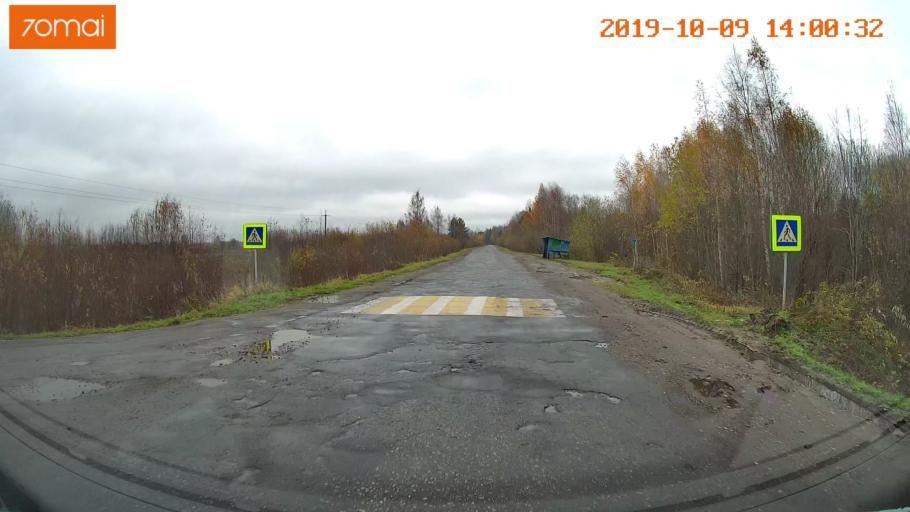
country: RU
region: Kostroma
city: Buy
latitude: 58.4397
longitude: 41.3369
